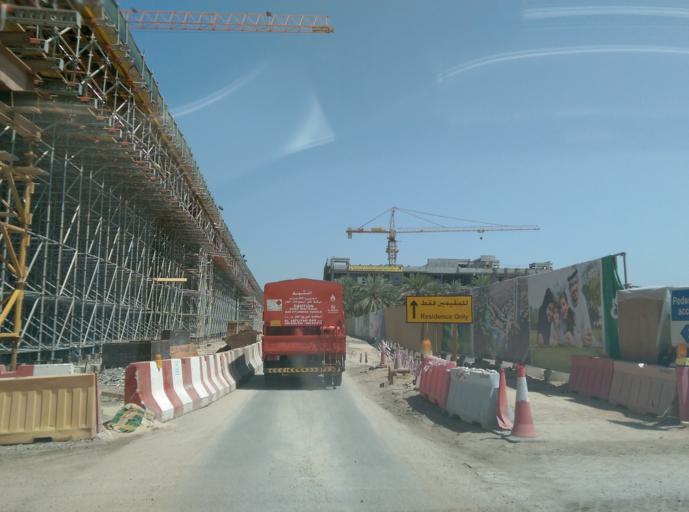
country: AE
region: Dubai
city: Dubai
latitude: 25.1954
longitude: 55.2359
